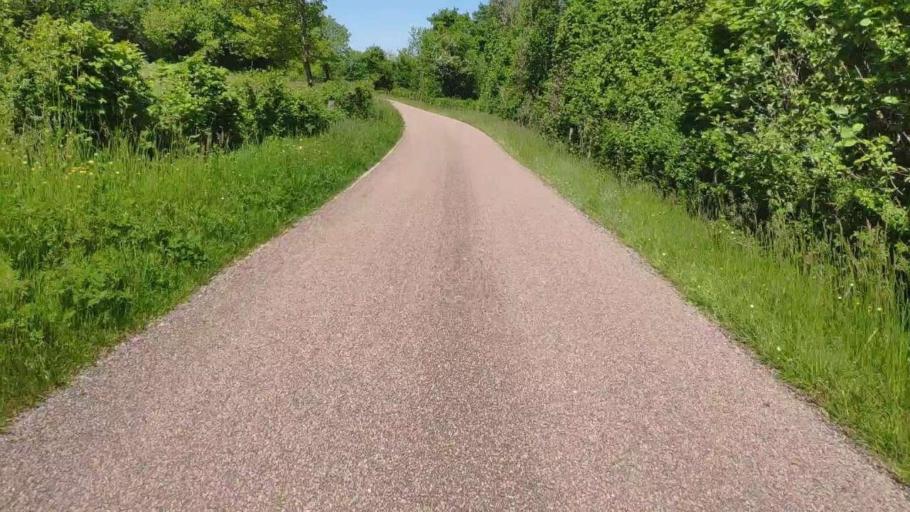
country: FR
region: Franche-Comte
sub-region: Departement du Jura
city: Poligny
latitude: 46.7338
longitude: 5.7245
